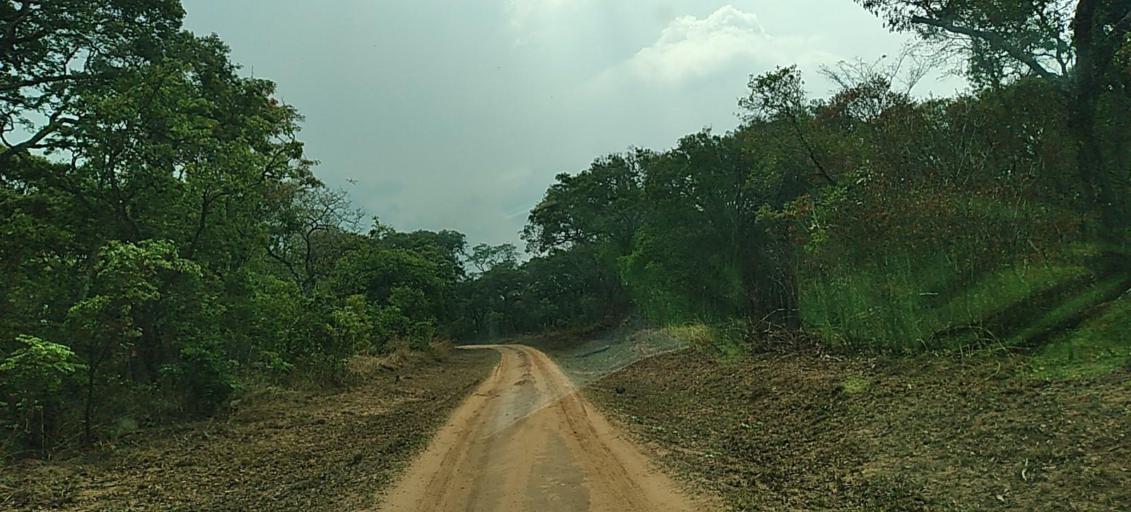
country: ZM
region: North-Western
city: Mwinilunga
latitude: -11.4666
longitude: 24.4748
